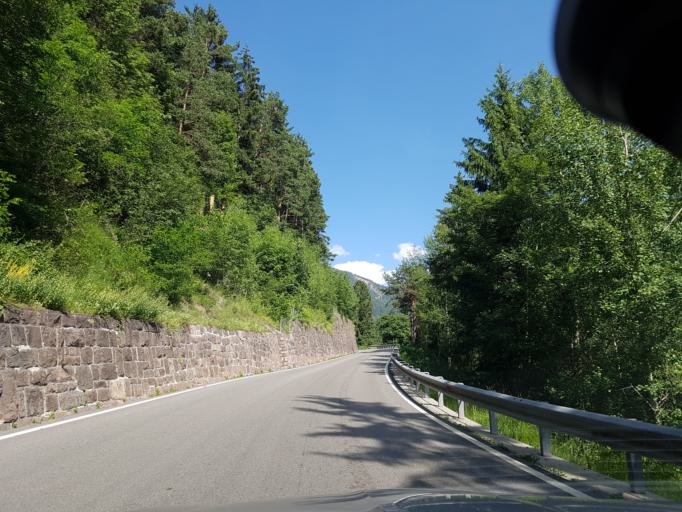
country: IT
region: Trentino-Alto Adige
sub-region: Bolzano
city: Laion
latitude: 46.5966
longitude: 11.6054
